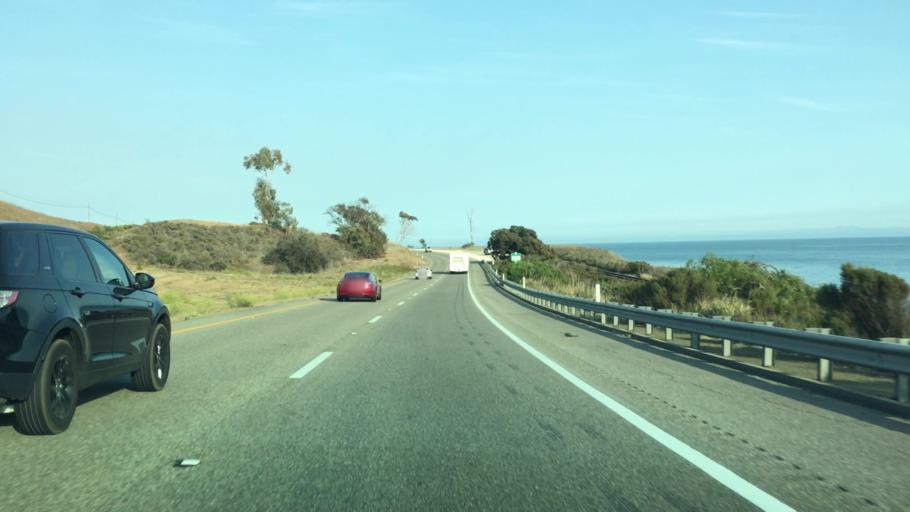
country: US
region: California
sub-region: Santa Barbara County
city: Solvang
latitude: 34.4645
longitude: -120.1006
